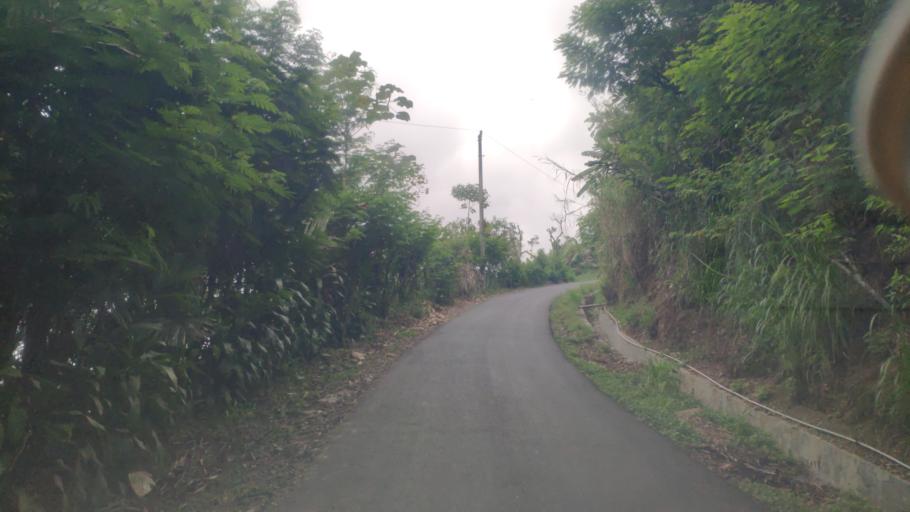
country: ID
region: Central Java
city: Wonosobo
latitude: -7.2940
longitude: 109.7702
